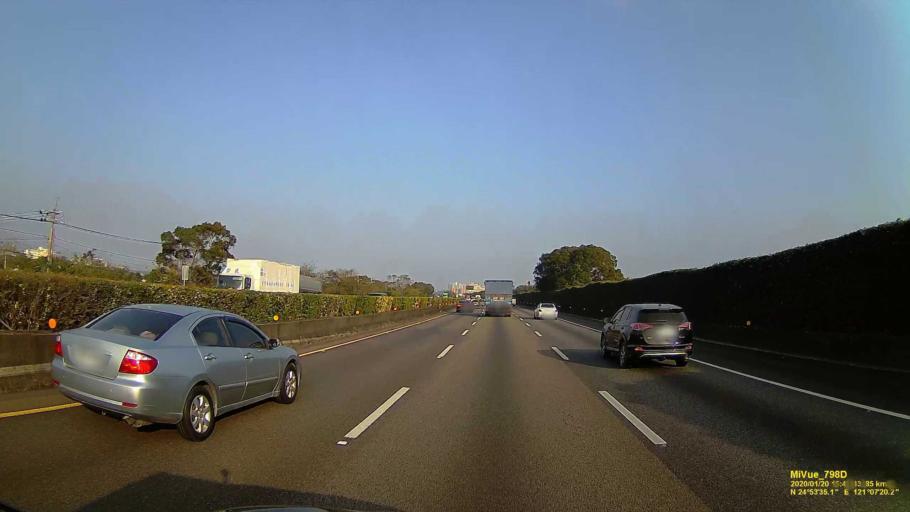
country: TW
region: Taiwan
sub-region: Hsinchu
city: Zhubei
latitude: 24.8931
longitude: 121.1232
